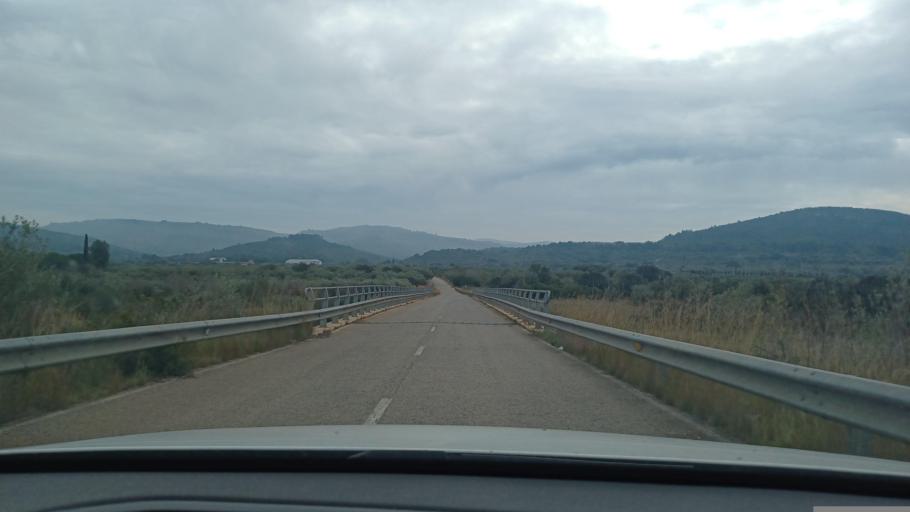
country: ES
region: Catalonia
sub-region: Provincia de Tarragona
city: Santa Barbara
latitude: 40.6659
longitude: 0.4519
